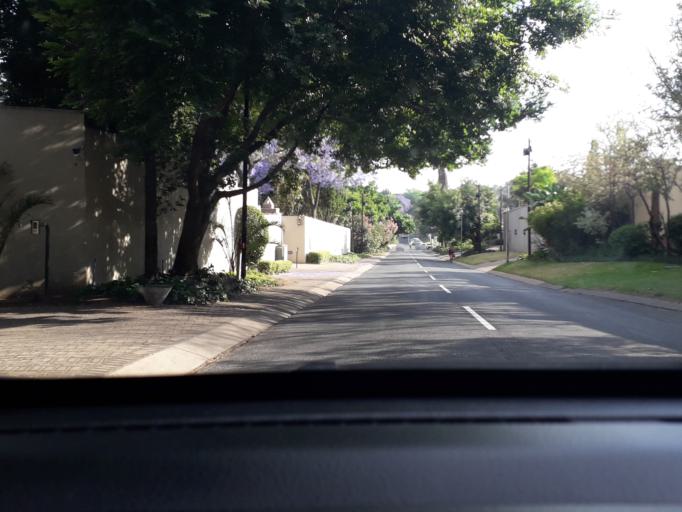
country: ZA
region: Gauteng
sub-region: City of Johannesburg Metropolitan Municipality
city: Modderfontein
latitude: -26.0840
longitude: 28.0571
